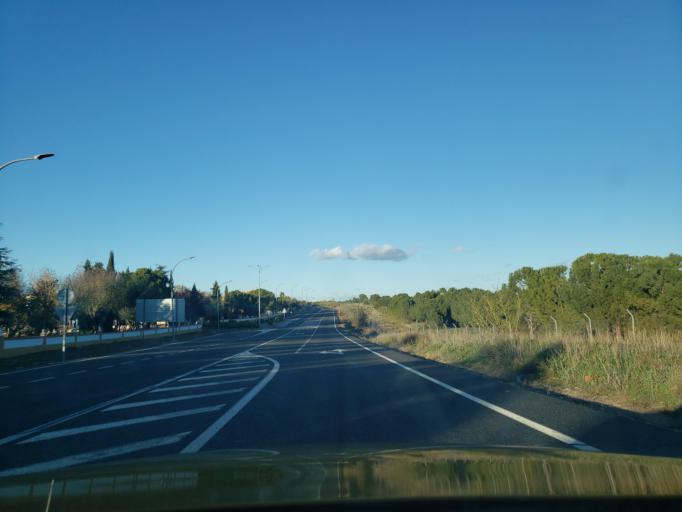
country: ES
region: Castille-La Mancha
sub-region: Province of Toledo
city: Cobisa
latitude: 39.8197
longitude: -4.0194
